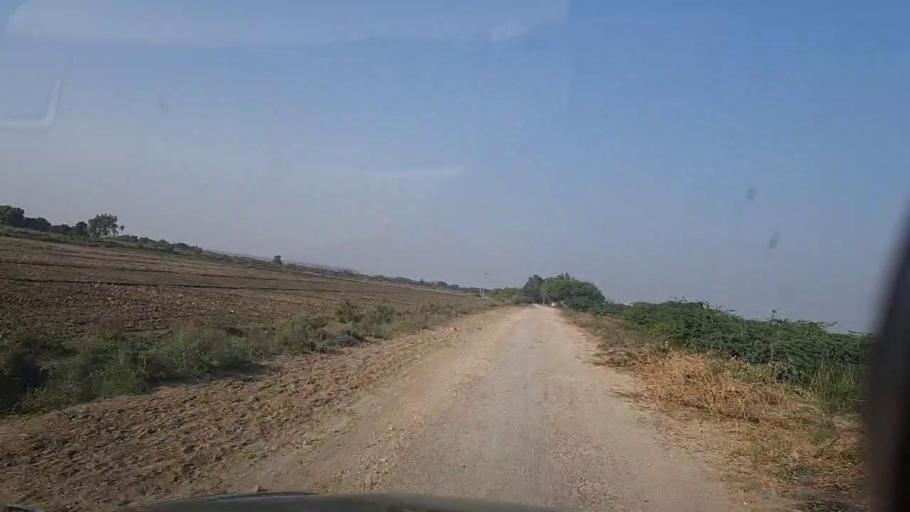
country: PK
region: Sindh
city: Thatta
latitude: 24.6010
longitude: 67.8743
